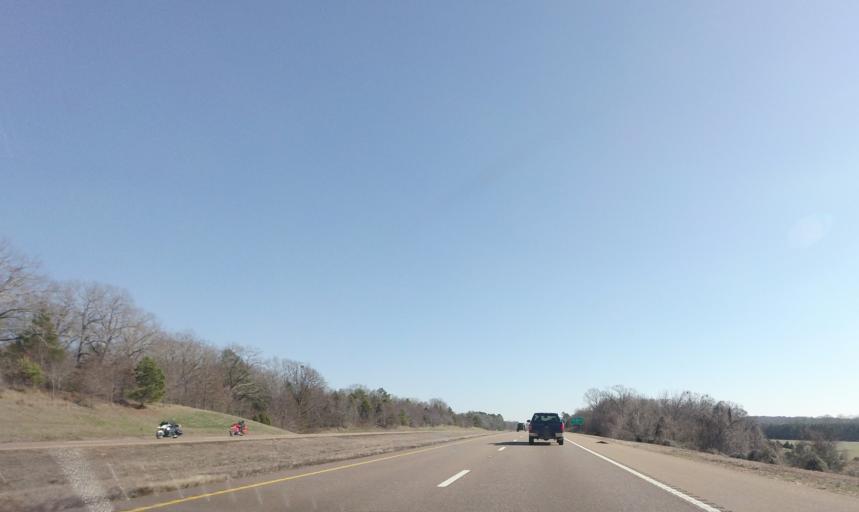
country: US
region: Mississippi
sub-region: Marshall County
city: Byhalia
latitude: 34.8327
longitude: -89.5885
